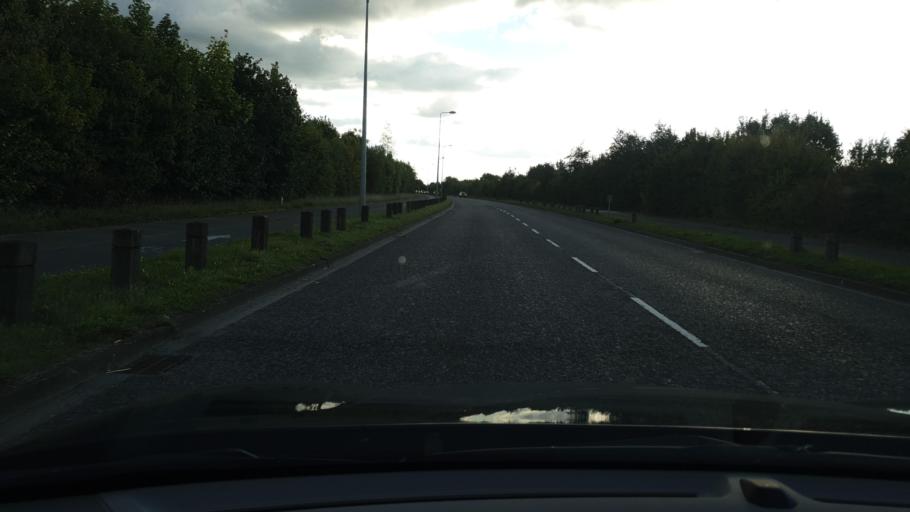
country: IE
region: Leinster
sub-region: Kildare
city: Naas
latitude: 53.2239
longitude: -6.6921
